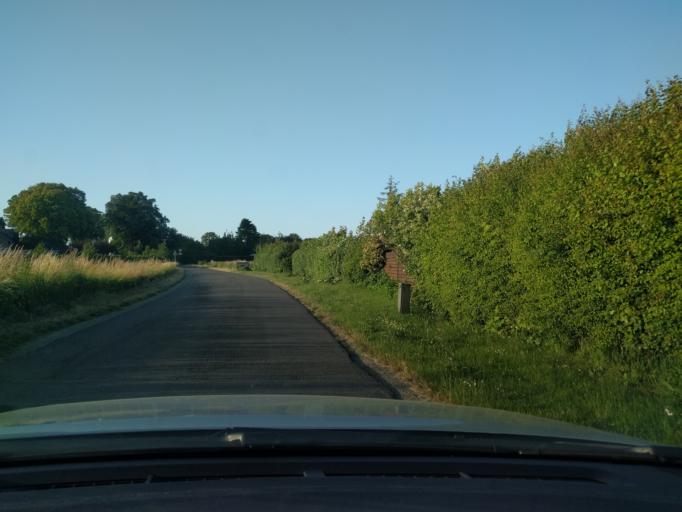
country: DK
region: Zealand
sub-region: Vordingborg Kommune
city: Stege
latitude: 54.9644
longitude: 12.2313
